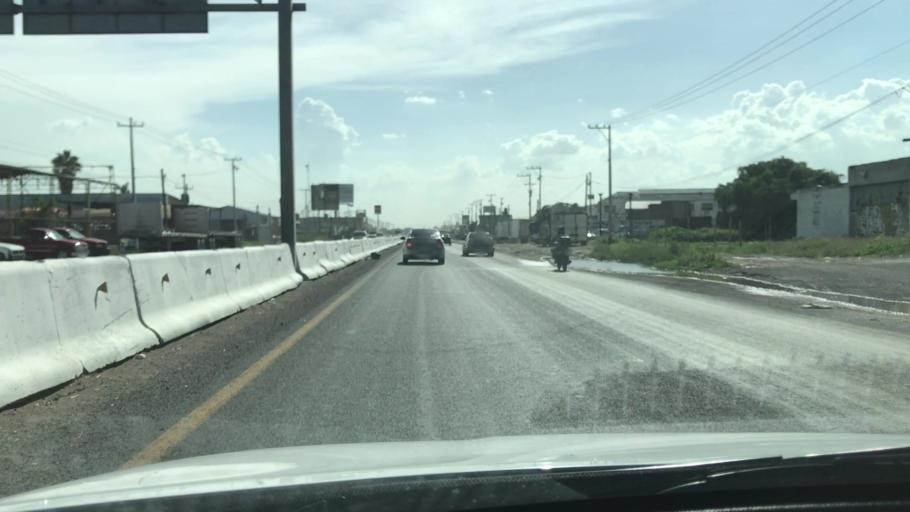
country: MX
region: Guanajuato
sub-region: Celaya
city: Colonia Pedro Maria Anaya
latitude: 20.5181
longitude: -100.8573
